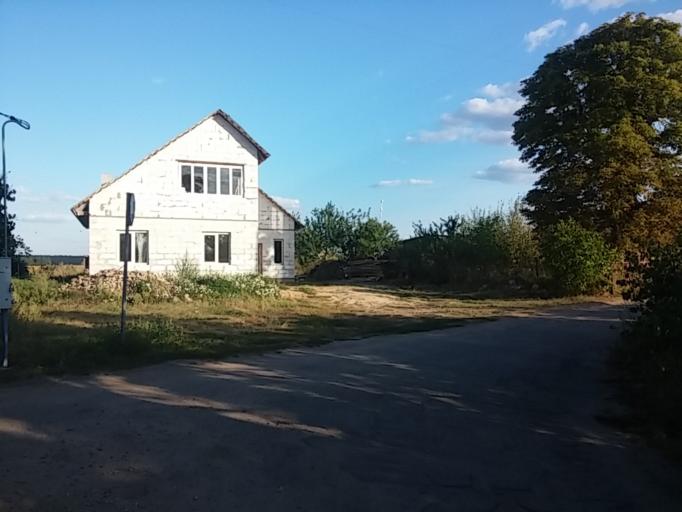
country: BY
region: Minsk
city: Chervyen'
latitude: 53.7771
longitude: 28.2668
